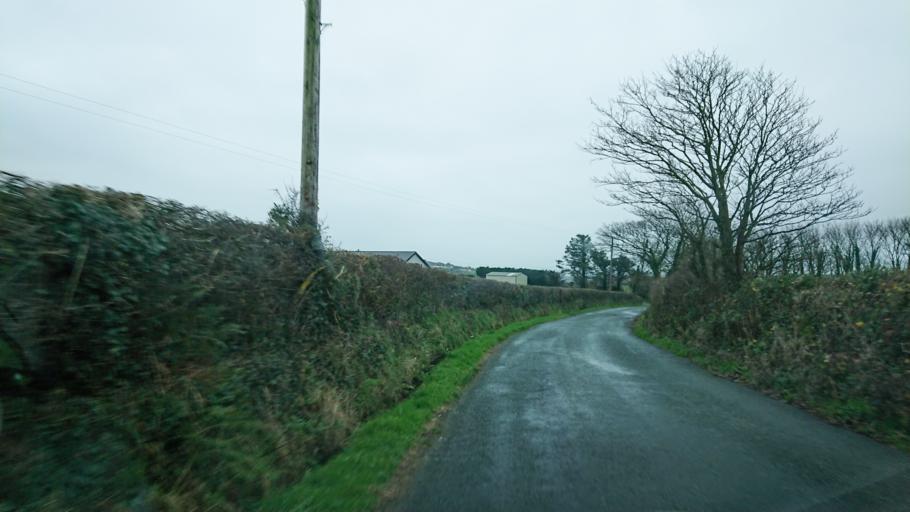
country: IE
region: Munster
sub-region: Waterford
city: Dunmore East
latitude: 52.1504
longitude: -7.0586
